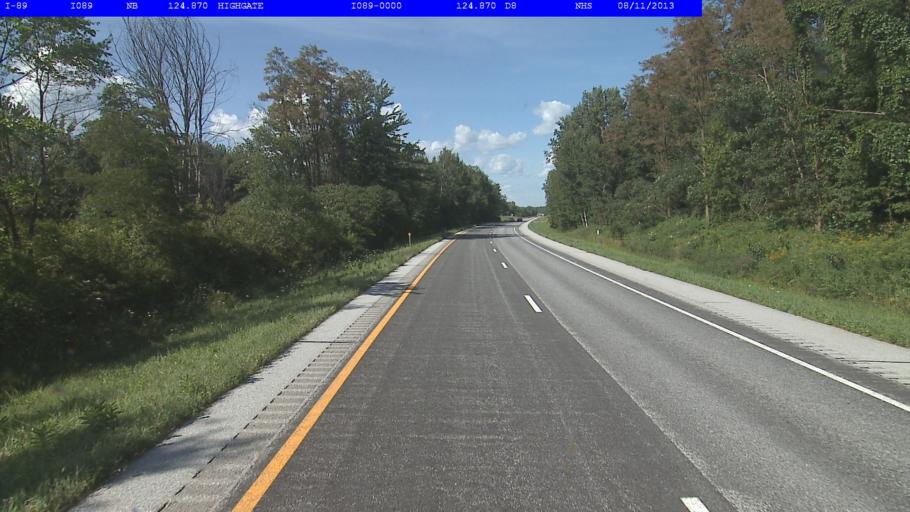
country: US
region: Vermont
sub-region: Franklin County
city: Swanton
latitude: 44.9433
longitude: -73.1146
